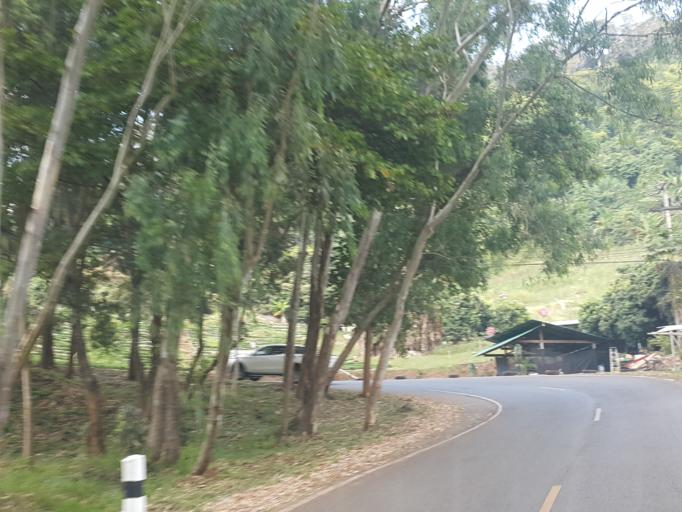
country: TH
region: Chiang Mai
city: Samoeng
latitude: 18.9180
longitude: 98.8215
